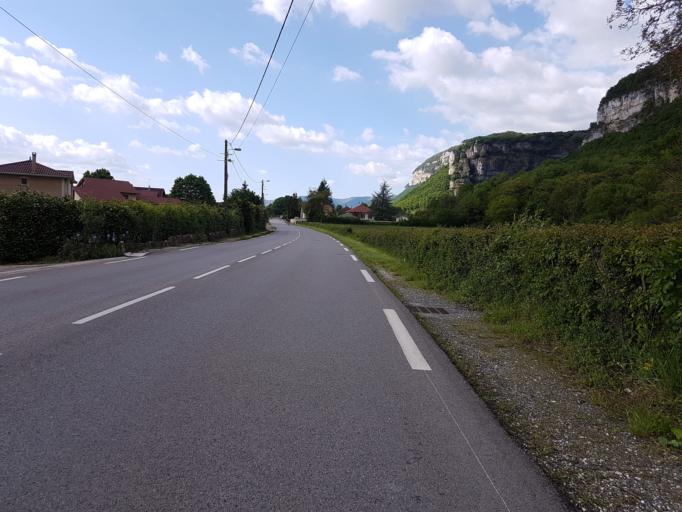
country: FR
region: Rhone-Alpes
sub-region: Departement de l'Isere
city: Bouvesse-Quirieu
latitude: 45.8005
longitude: 5.4571
